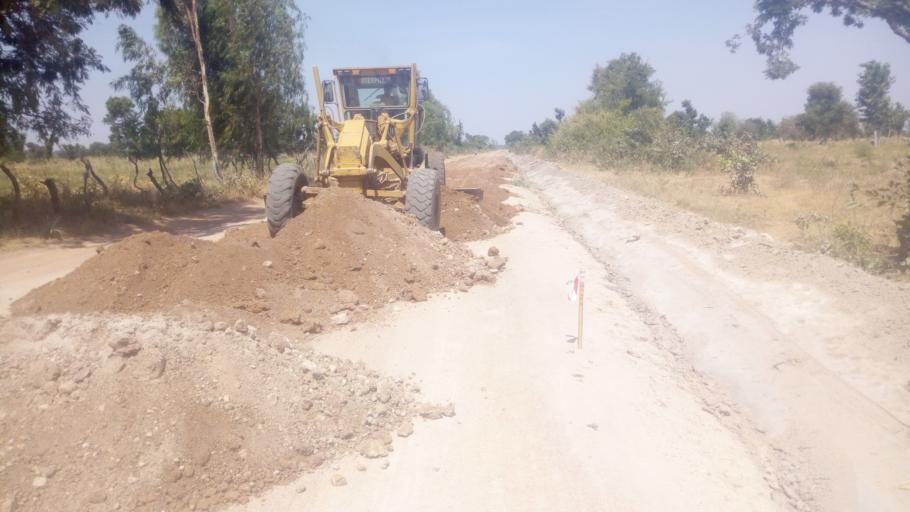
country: NG
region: Adamawa
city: Yola
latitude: 9.1665
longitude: 12.4024
